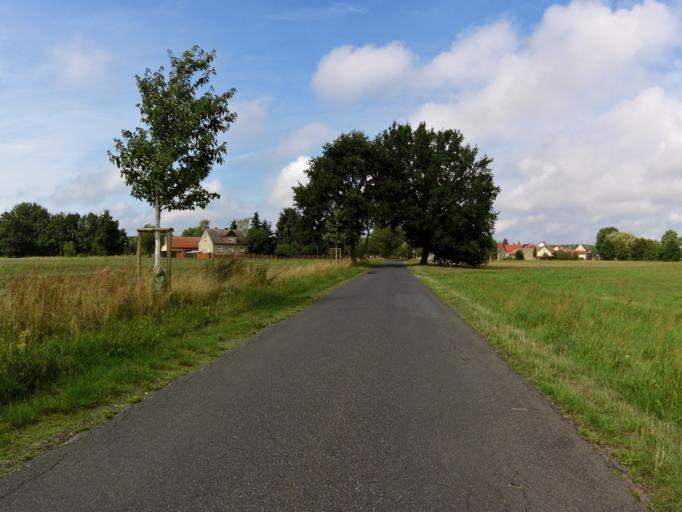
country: DE
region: Brandenburg
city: Storkow
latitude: 52.2746
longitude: 13.9301
